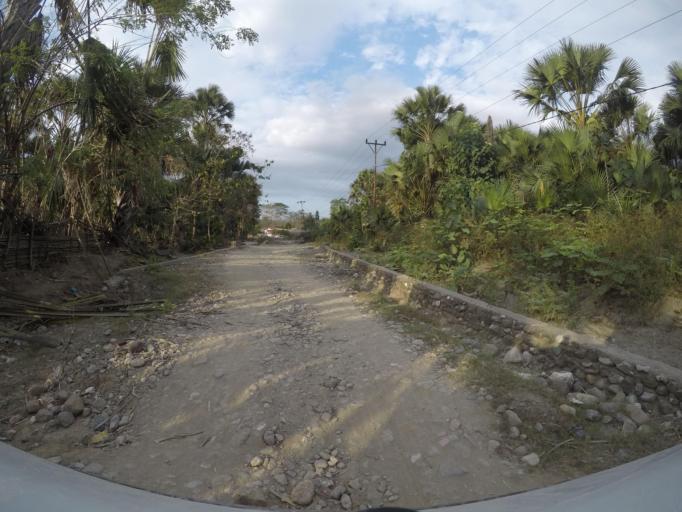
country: TL
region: Bobonaro
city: Maliana
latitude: -8.8650
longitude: 125.2151
